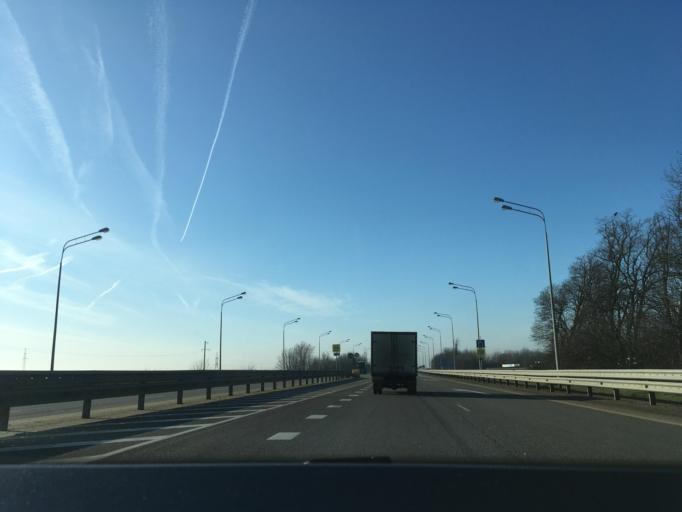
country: RU
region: Krasnodarskiy
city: Agronom
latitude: 45.1754
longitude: 39.1027
